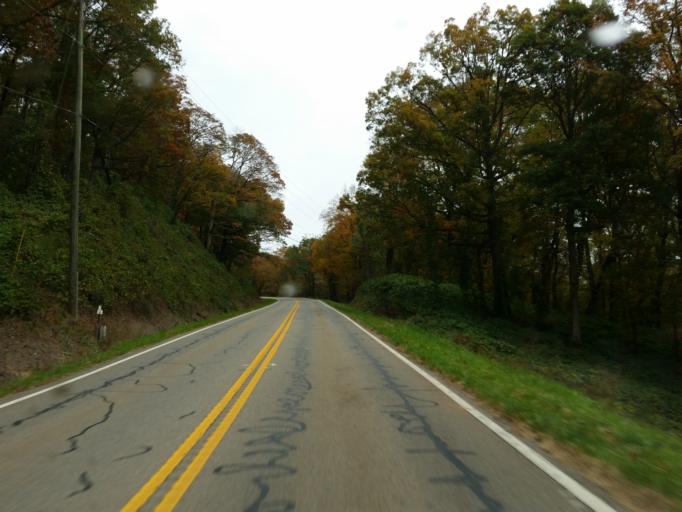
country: US
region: Georgia
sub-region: Pickens County
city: Jasper
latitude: 34.5336
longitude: -84.3845
